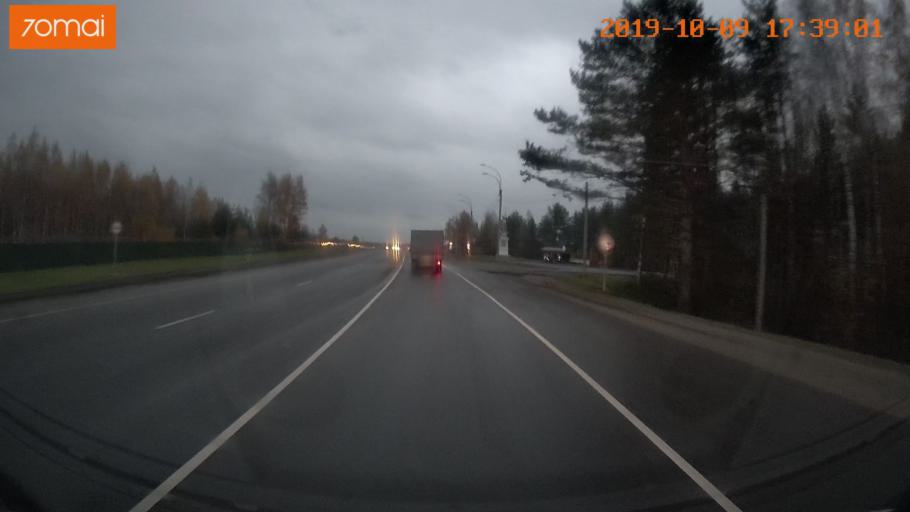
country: RU
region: Ivanovo
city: Bogorodskoye
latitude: 57.0645
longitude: 40.9535
